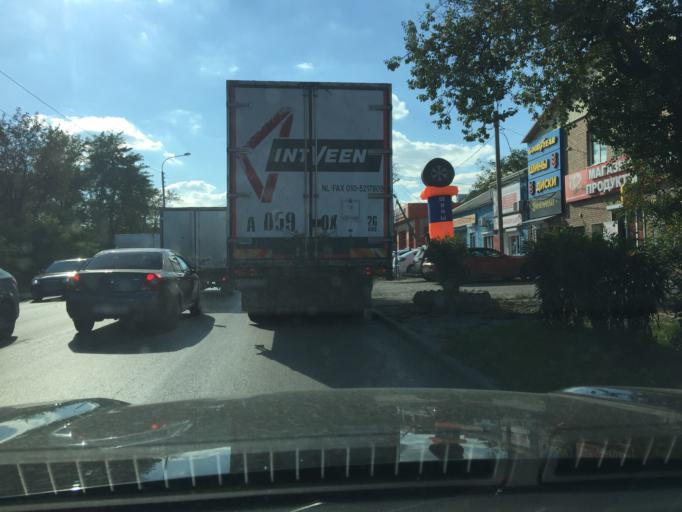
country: RU
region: Rostov
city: Rostov-na-Donu
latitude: 47.2430
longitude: 39.6436
